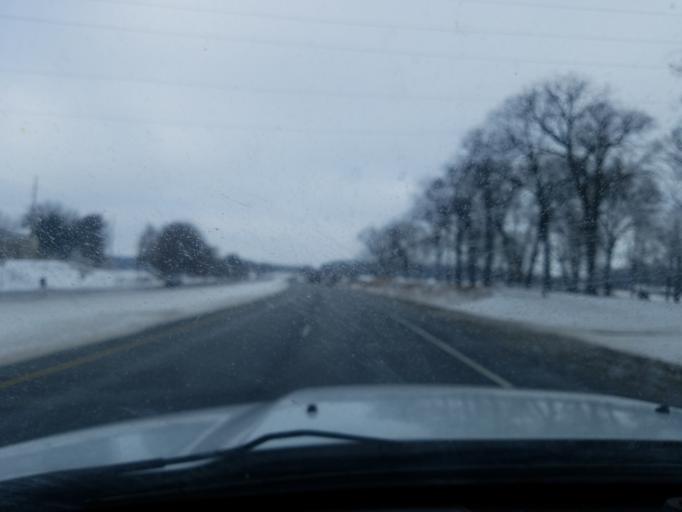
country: US
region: Indiana
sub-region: Marshall County
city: Plymouth
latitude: 41.2902
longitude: -86.2710
